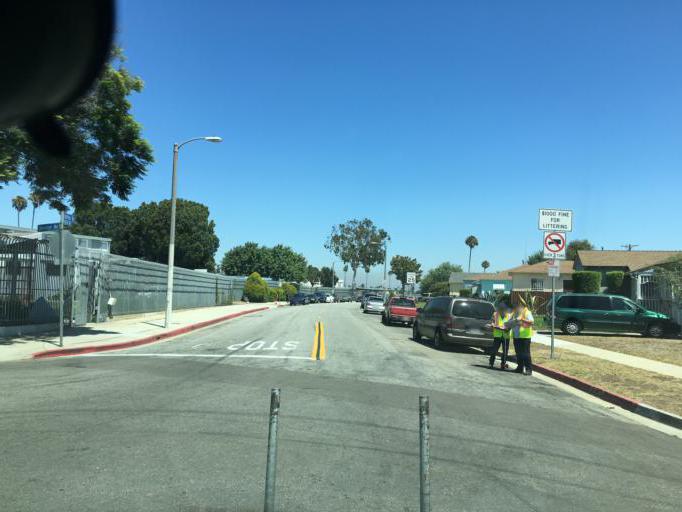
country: US
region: California
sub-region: Los Angeles County
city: Westmont
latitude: 33.9353
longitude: -118.3047
